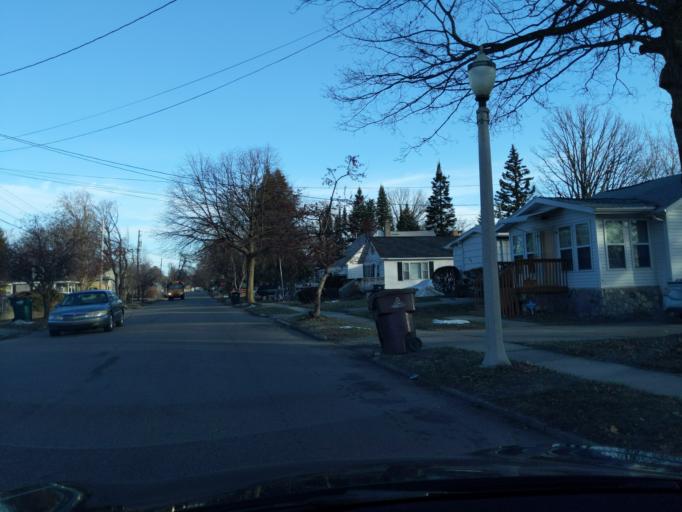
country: US
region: Michigan
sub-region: Ingham County
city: Lansing
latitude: 42.6935
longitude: -84.5619
